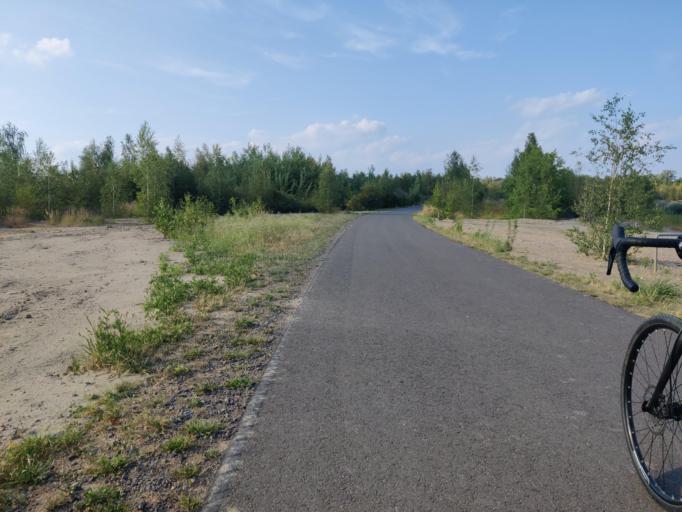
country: DE
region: Saxony
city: Neukieritzsch
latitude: 51.1763
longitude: 12.4329
